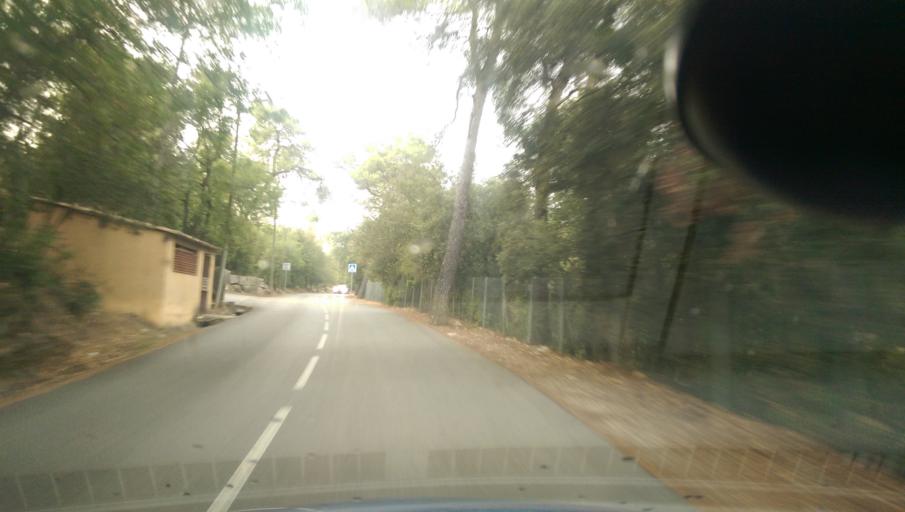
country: FR
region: Provence-Alpes-Cote d'Azur
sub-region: Departement des Alpes-Maritimes
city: Valbonne
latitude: 43.6396
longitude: 7.0397
